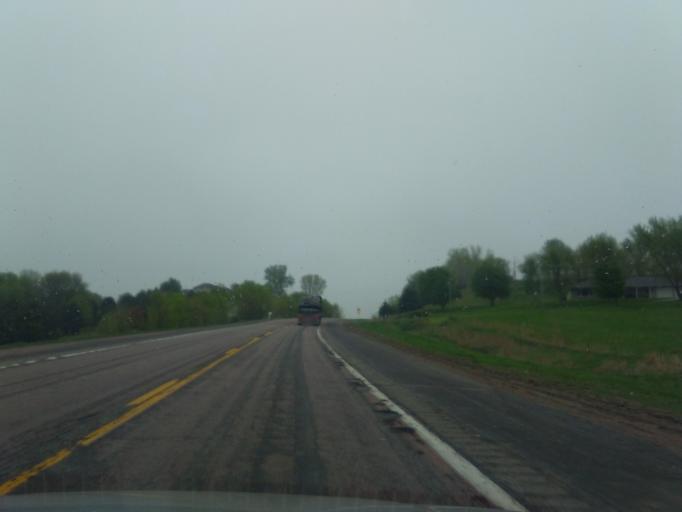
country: US
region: Nebraska
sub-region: Burt County
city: Oakland
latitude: 41.8201
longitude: -96.4703
